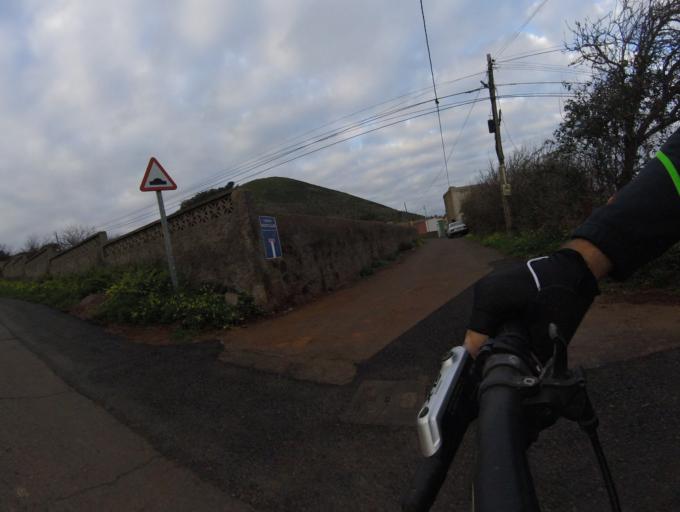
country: ES
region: Canary Islands
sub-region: Provincia de Santa Cruz de Tenerife
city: La Laguna
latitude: 28.4512
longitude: -16.3563
